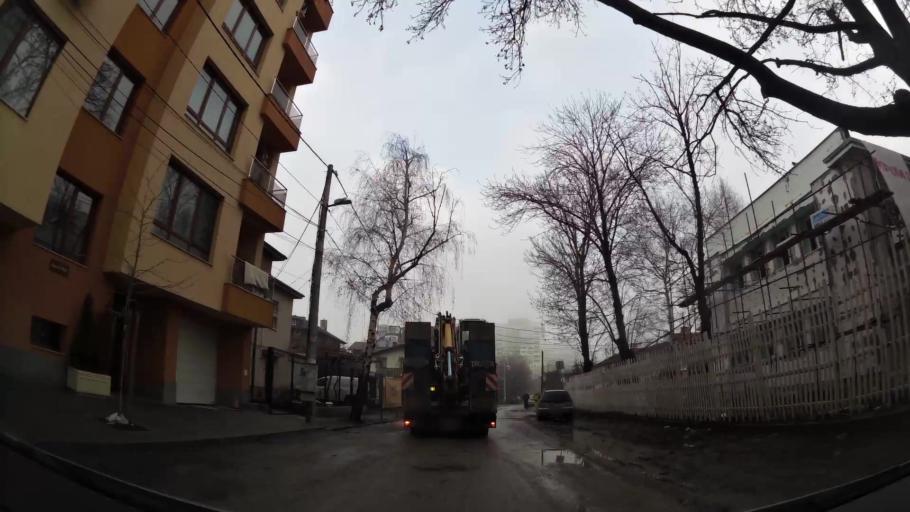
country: BG
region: Sofia-Capital
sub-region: Stolichna Obshtina
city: Sofia
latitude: 42.7313
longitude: 23.2993
